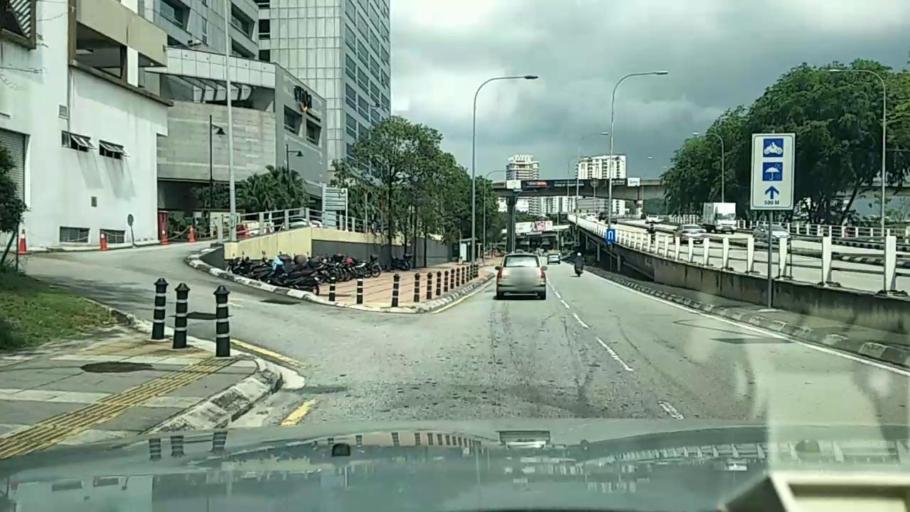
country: MY
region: Kuala Lumpur
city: Kuala Lumpur
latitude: 3.1268
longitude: 101.6765
